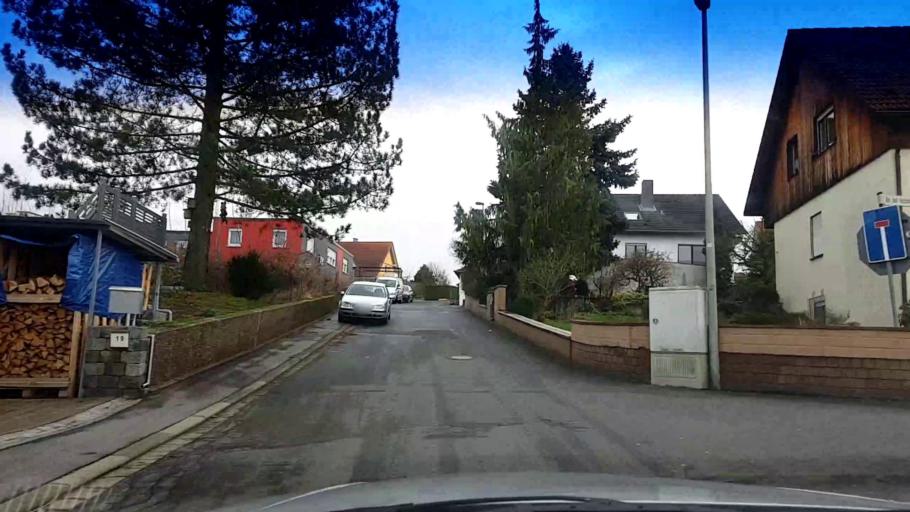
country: DE
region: Bavaria
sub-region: Upper Franconia
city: Litzendorf
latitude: 49.9072
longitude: 10.9928
